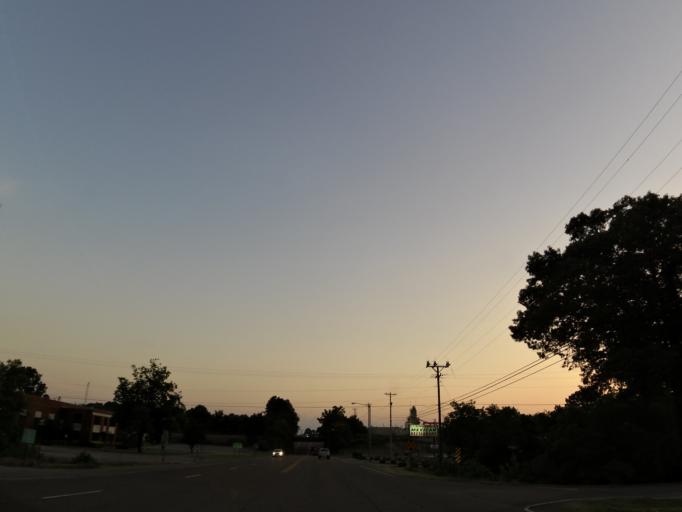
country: US
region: Tennessee
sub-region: Carroll County
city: McKenzie
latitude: 36.1274
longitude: -88.5120
